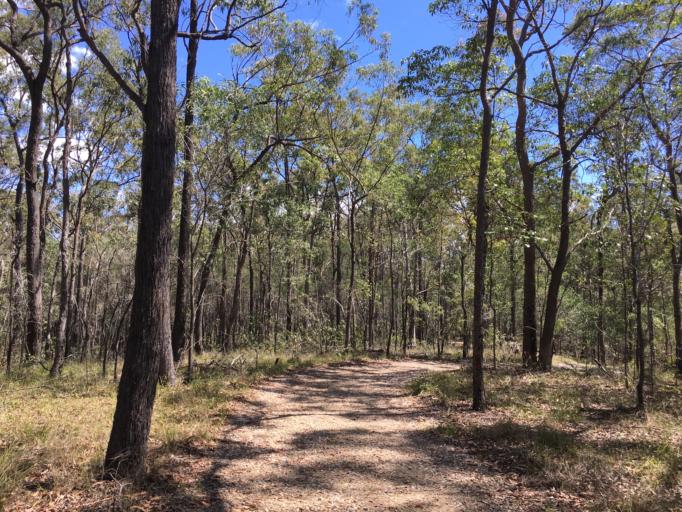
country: AU
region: Queensland
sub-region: Logan
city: Woodridge
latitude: -27.6264
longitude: 153.0877
